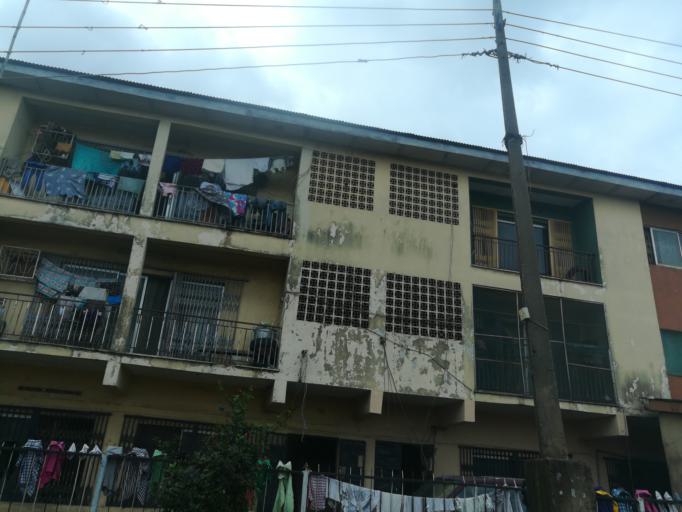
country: NG
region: Lagos
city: Agege
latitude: 6.6212
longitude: 3.3350
